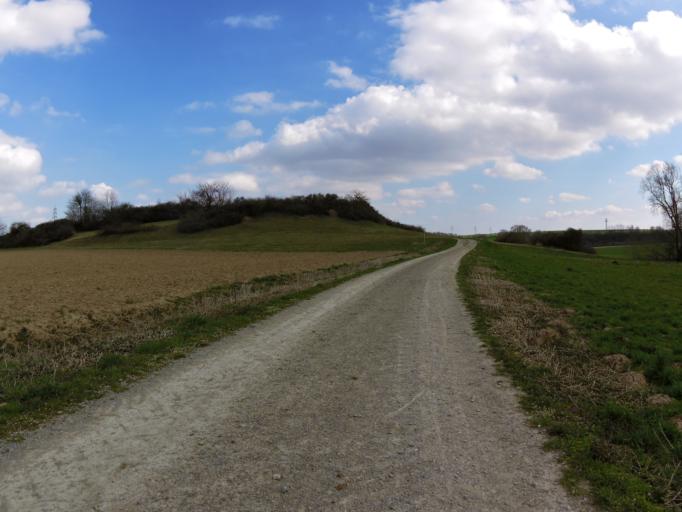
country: DE
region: Bavaria
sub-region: Regierungsbezirk Unterfranken
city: Biebelried
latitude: 49.7448
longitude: 10.0903
